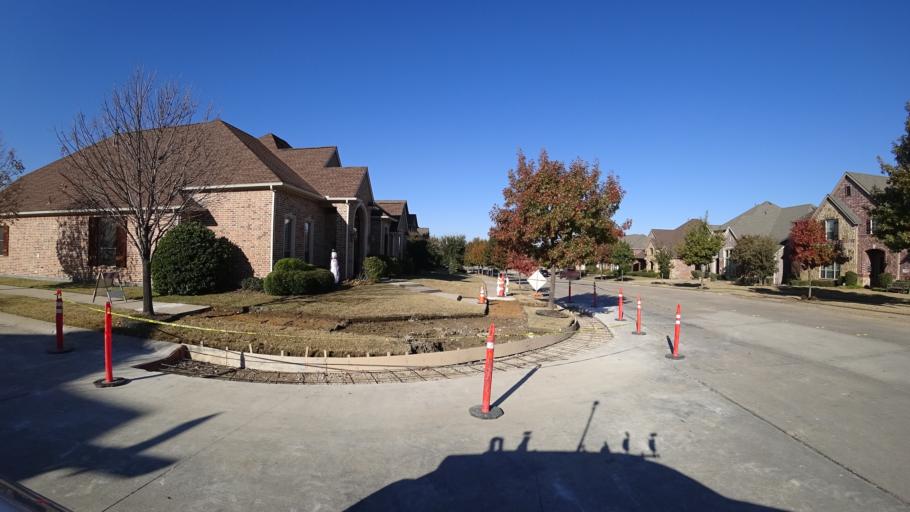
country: US
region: Texas
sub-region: Denton County
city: The Colony
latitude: 33.0434
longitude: -96.9109
